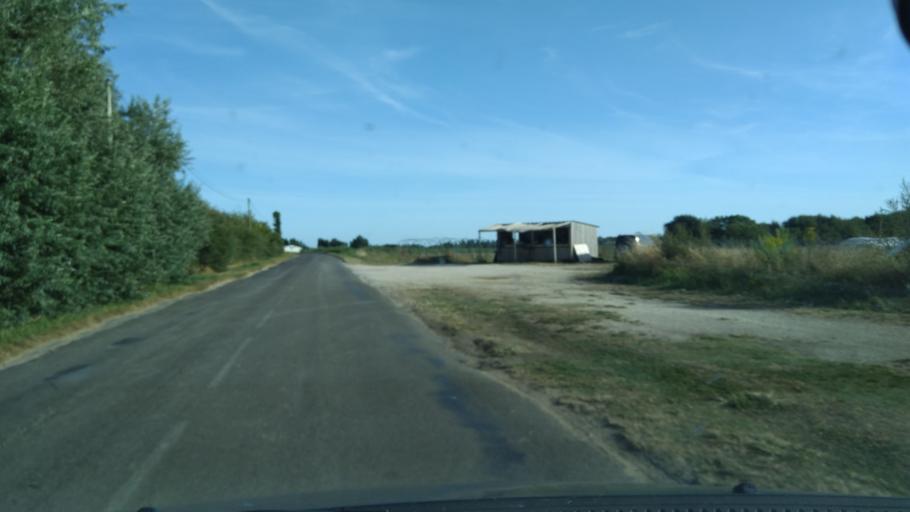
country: FR
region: Poitou-Charentes
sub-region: Departement de la Charente-Maritime
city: Dolus-d'Oleron
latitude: 45.9373
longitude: -1.3384
